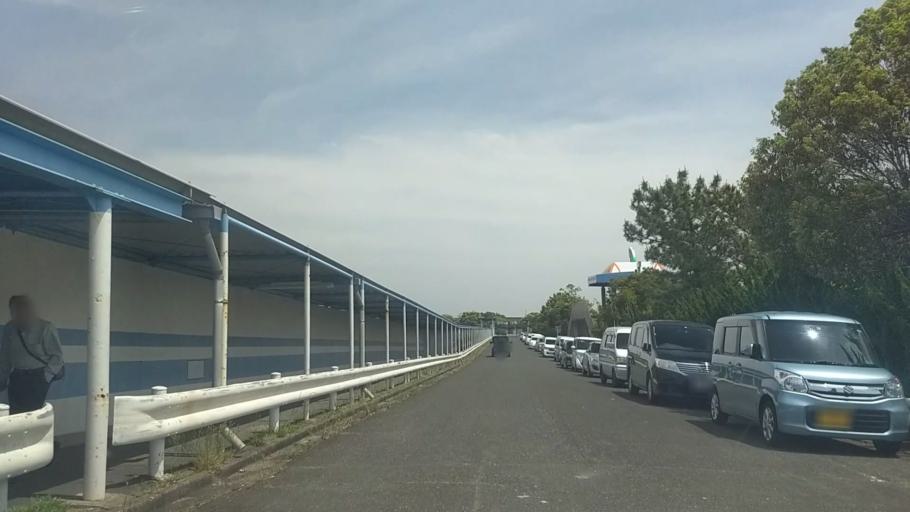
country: JP
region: Shizuoka
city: Kosai-shi
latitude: 34.6960
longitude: 137.5725
